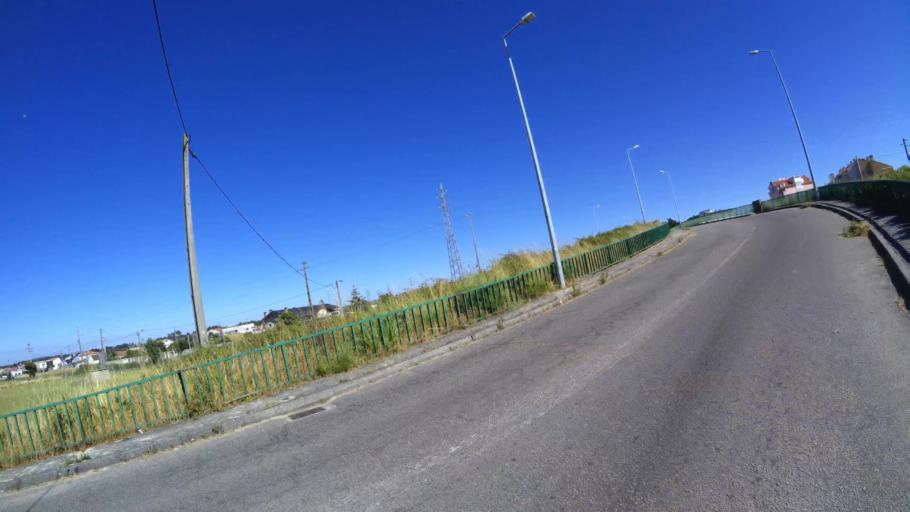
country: PT
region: Aveiro
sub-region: Aveiro
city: Aveiro
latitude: 40.6564
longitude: -8.6237
